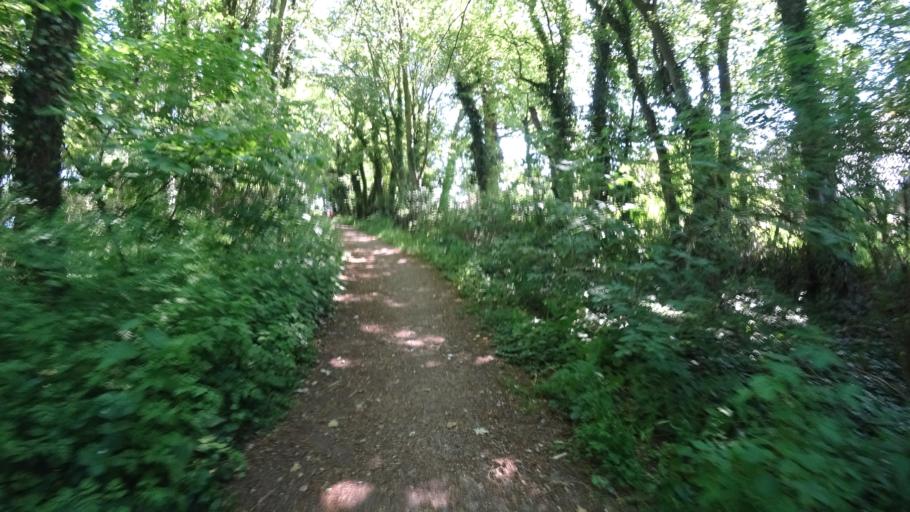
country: DE
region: North Rhine-Westphalia
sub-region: Regierungsbezirk Detmold
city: Rheda-Wiedenbruck
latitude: 51.8571
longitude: 8.3432
